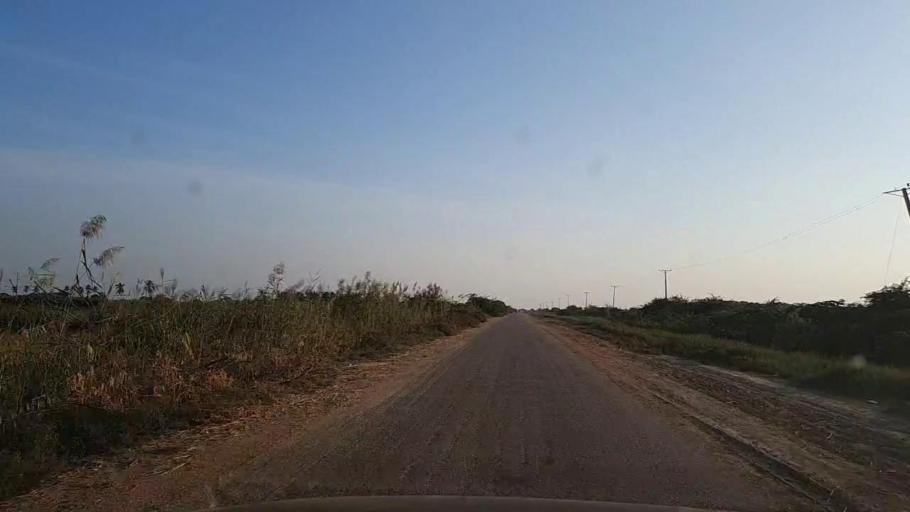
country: PK
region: Sindh
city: Thatta
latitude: 24.6469
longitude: 67.9124
